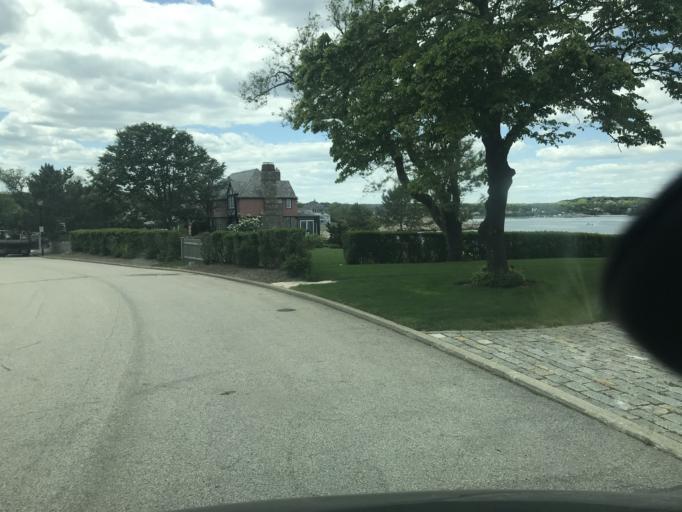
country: US
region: Massachusetts
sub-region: Essex County
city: Rockport
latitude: 42.6582
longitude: -70.6051
